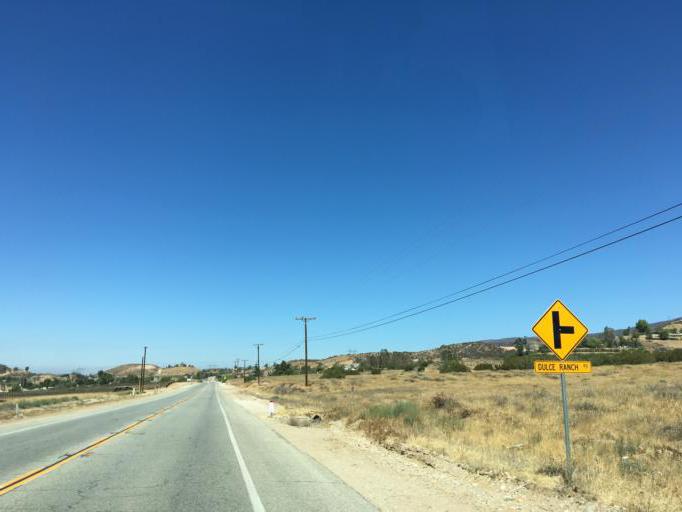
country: US
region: California
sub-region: Los Angeles County
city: Agua Dulce
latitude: 34.5202
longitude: -118.3088
